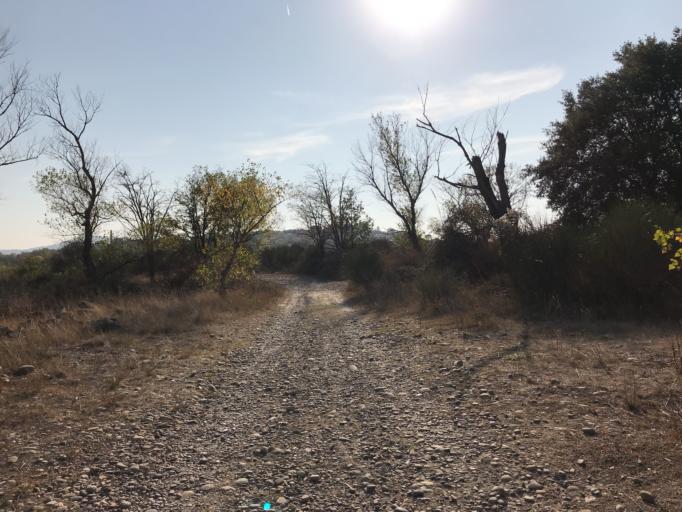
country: FR
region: Provence-Alpes-Cote d'Azur
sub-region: Departement des Bouches-du-Rhone
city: Mallemort
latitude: 43.7372
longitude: 5.1859
